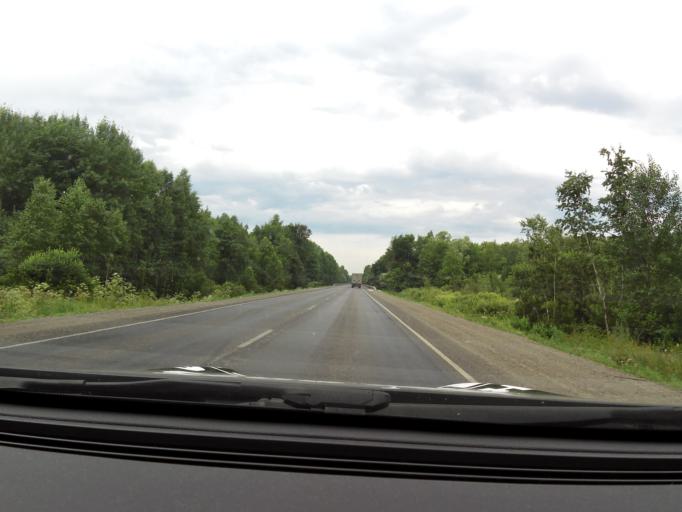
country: RU
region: Bashkortostan
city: Ulu-Telyak
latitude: 54.8317
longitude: 56.9557
